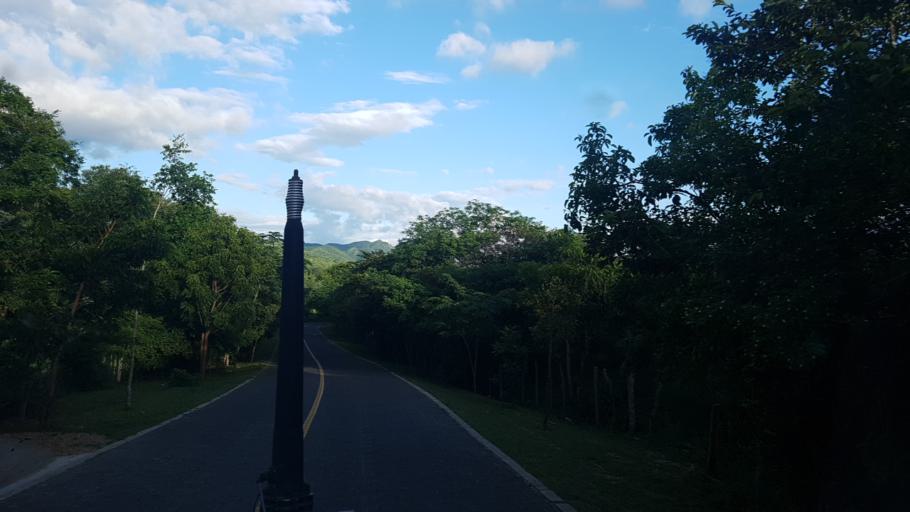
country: NI
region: Nueva Segovia
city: Ocotal
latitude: 13.6434
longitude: -86.5984
